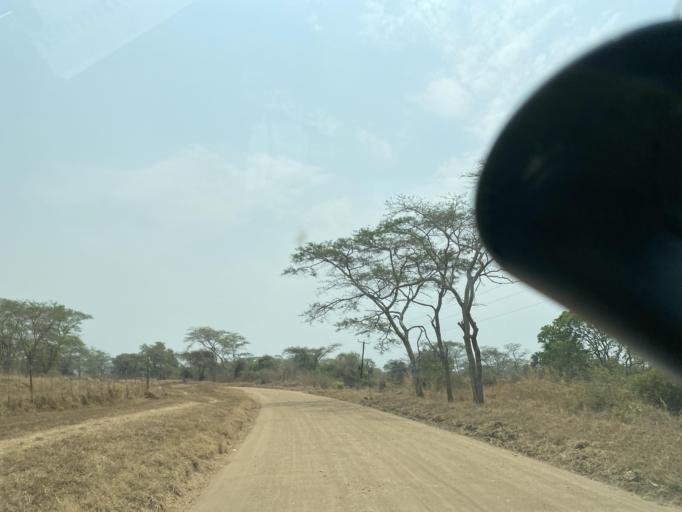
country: ZM
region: Lusaka
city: Kafue
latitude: -15.5888
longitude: 28.1163
